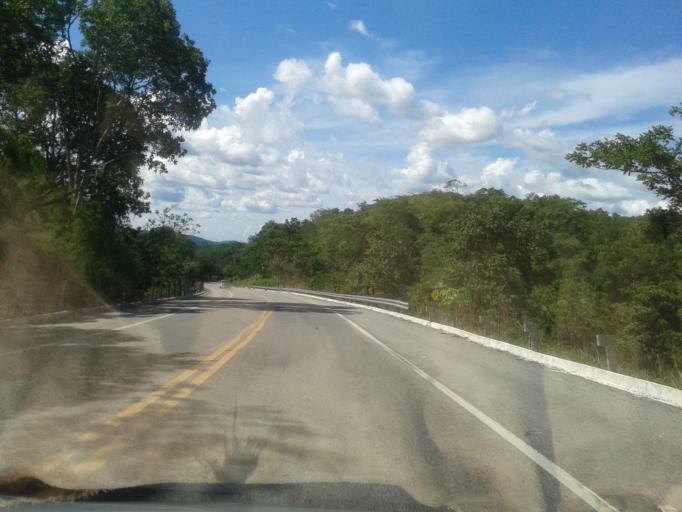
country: BR
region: Goias
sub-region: Goias
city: Goias
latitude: -15.6656
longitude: -50.2163
